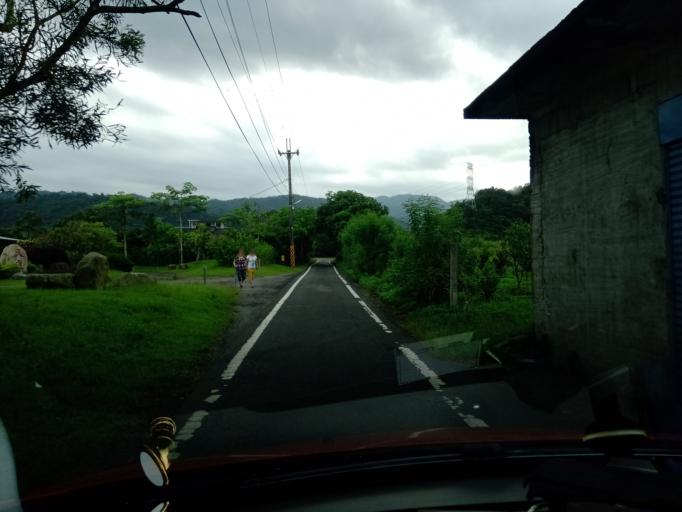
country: TW
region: Taiwan
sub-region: Yilan
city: Yilan
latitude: 24.7814
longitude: 121.7165
